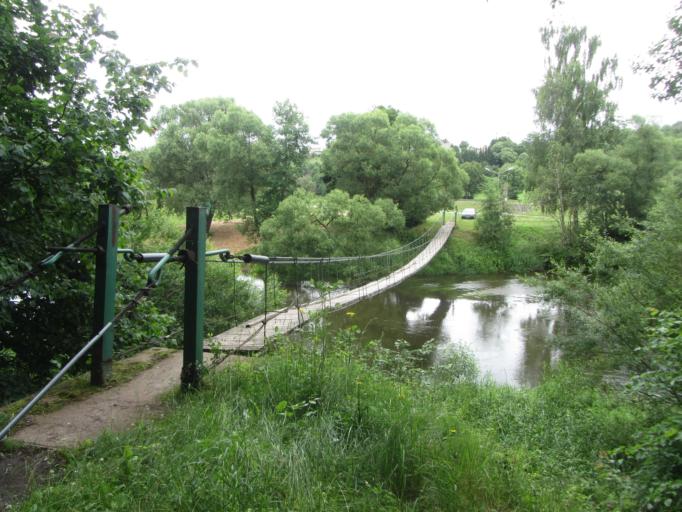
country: LT
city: Ariogala
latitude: 55.2619
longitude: 23.4589
